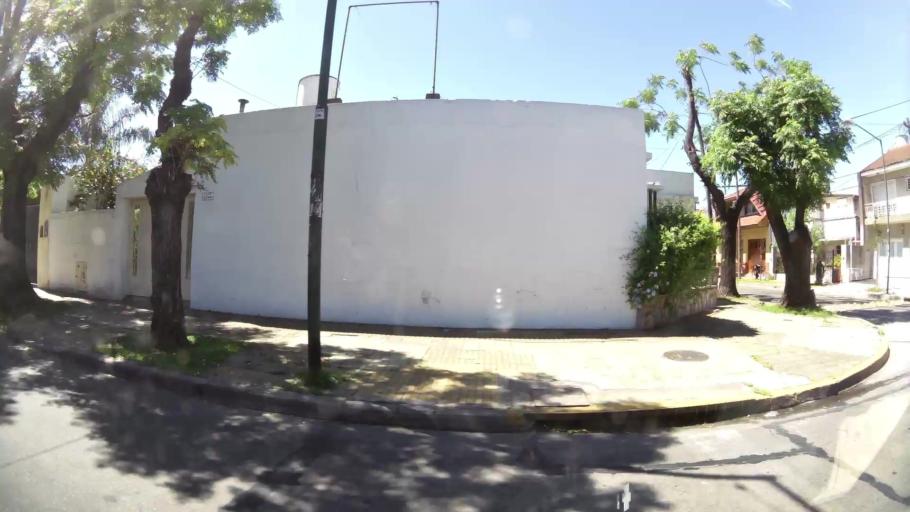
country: AR
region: Buenos Aires
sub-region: Partido de General San Martin
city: General San Martin
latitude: -34.5282
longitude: -58.5534
